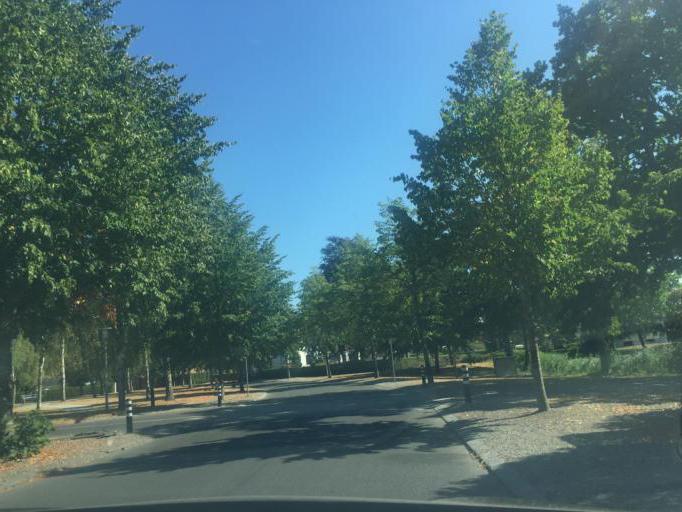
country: DK
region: Central Jutland
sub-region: Hedensted Kommune
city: Juelsminde
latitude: 55.7141
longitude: 10.0085
